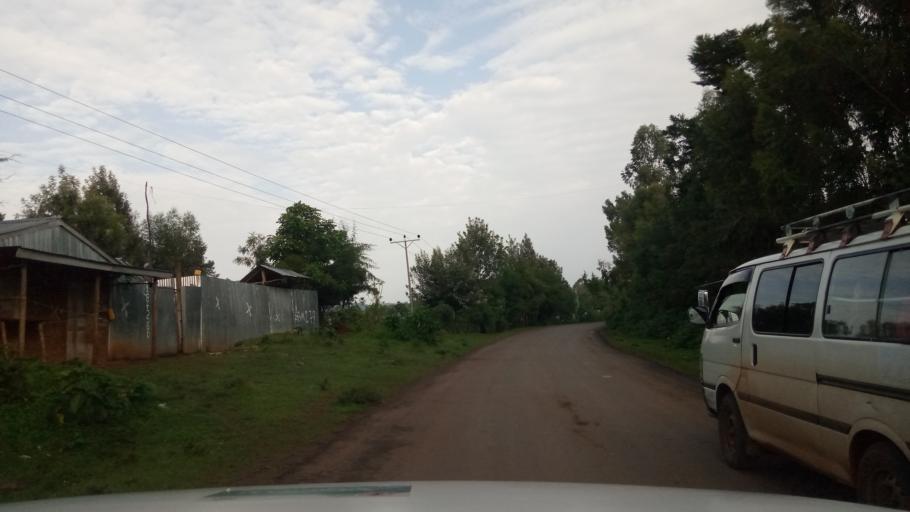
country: ET
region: Oromiya
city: Jima
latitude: 7.7411
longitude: 36.7412
